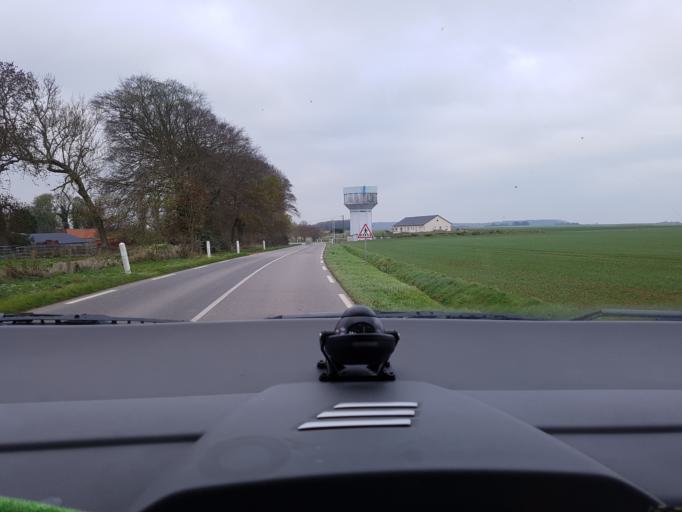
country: FR
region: Haute-Normandie
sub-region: Departement de la Seine-Maritime
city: Le Treport
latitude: 50.0302
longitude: 1.3531
